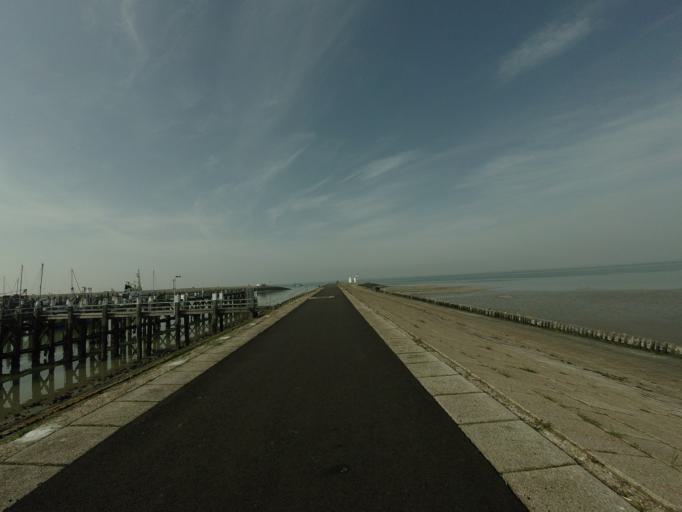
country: NL
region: Zeeland
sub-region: Gemeente Terneuzen
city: Terneuzen
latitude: 51.3403
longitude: 3.8296
